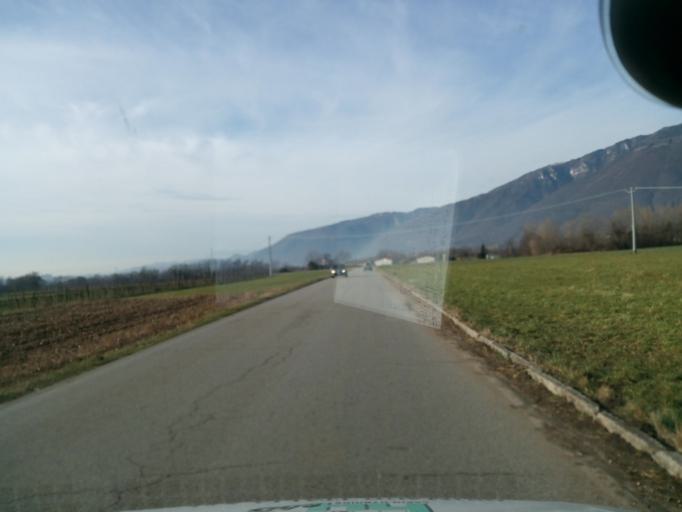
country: IT
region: Veneto
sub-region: Provincia di Treviso
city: Crespano del Grappa
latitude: 45.8161
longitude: 11.8330
